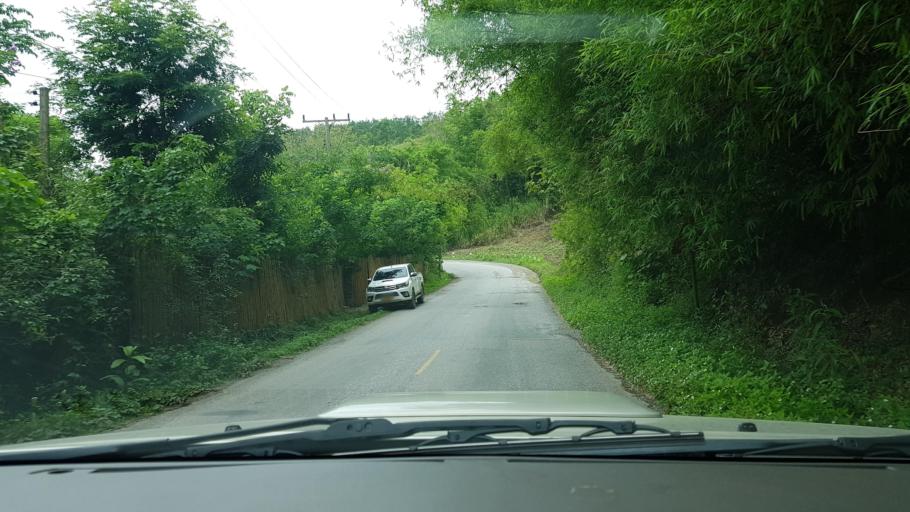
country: LA
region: Oudomxai
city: Muang Xay
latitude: 20.7354
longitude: 102.0247
